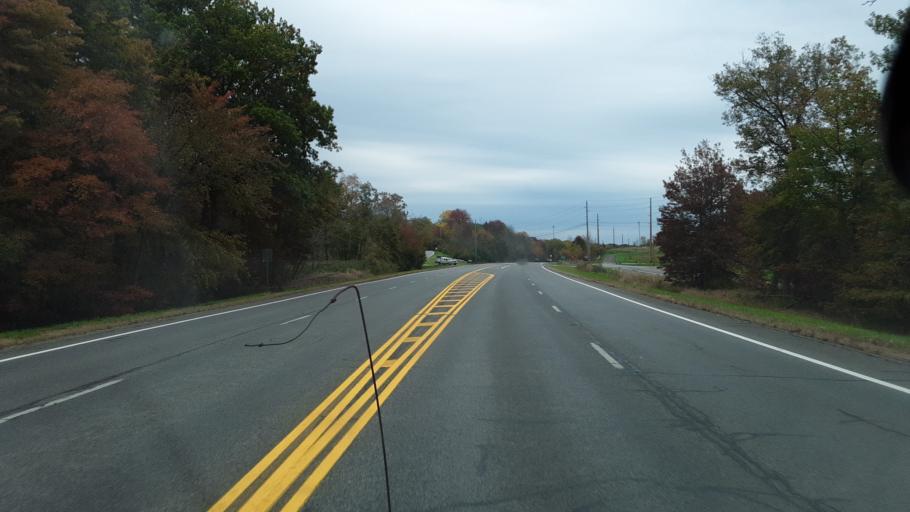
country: US
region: Ohio
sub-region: Portage County
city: Ravenna
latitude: 41.1789
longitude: -81.2419
